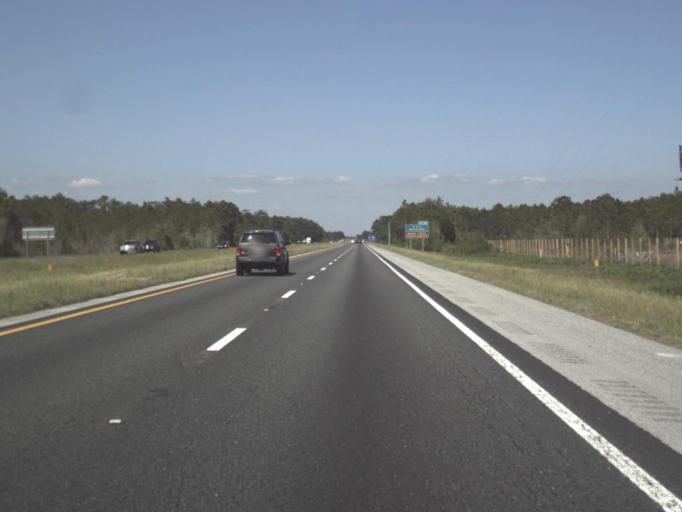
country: US
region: Florida
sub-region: Santa Rosa County
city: Bagdad
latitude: 30.5578
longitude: -87.0469
